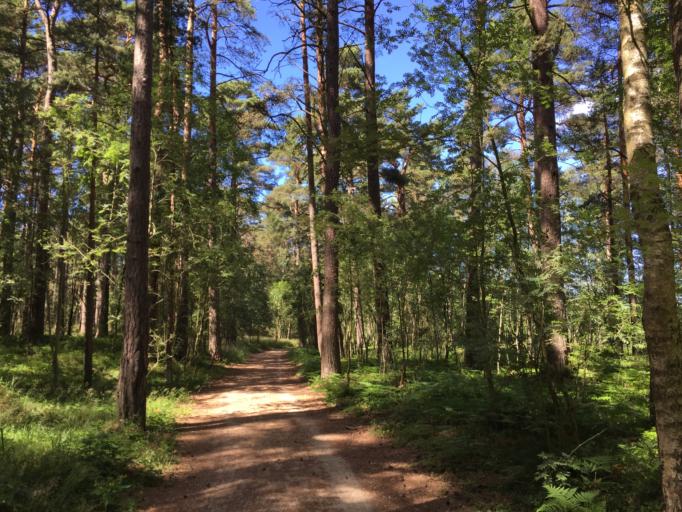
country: LV
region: Ventspils
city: Ventspils
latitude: 57.4474
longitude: 21.6299
